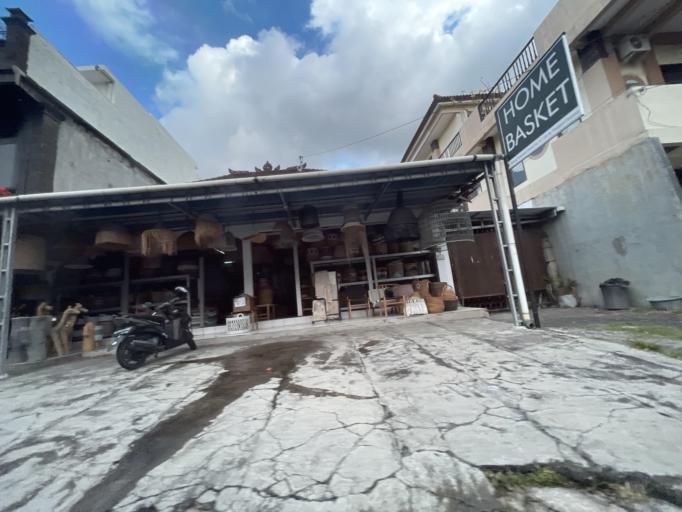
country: ID
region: Bali
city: Kuta
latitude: -8.6770
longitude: 115.1737
